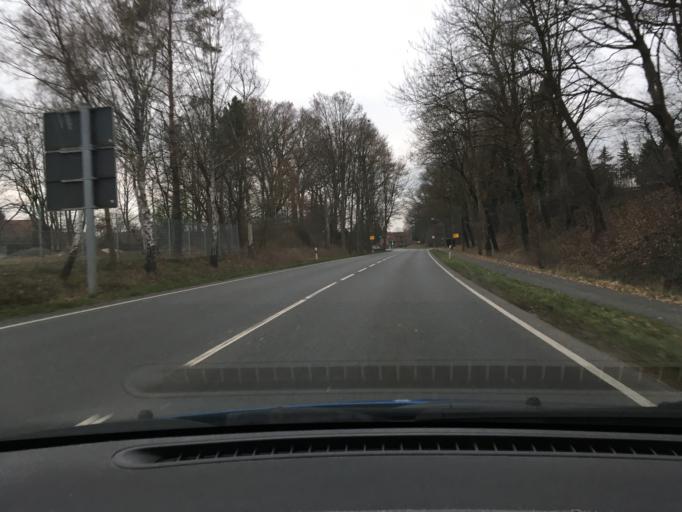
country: DE
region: Lower Saxony
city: Bomlitz
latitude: 52.8657
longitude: 9.6328
